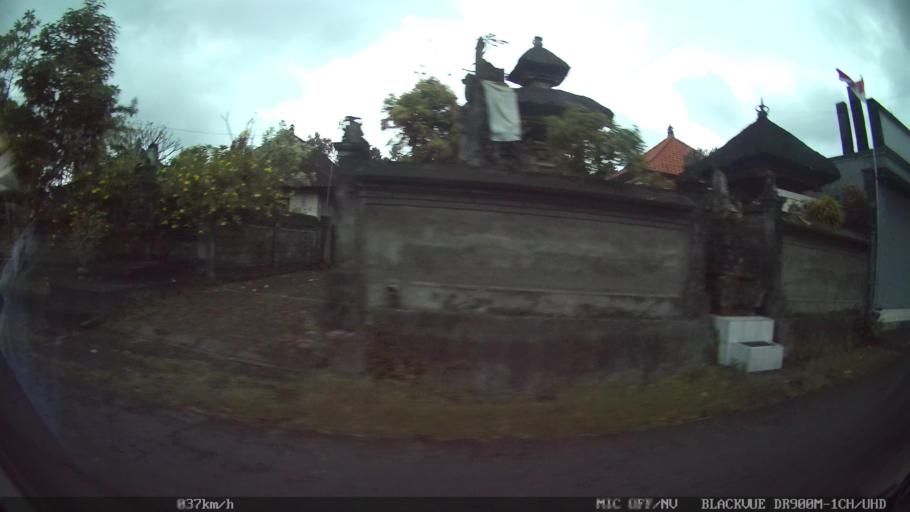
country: ID
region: Bali
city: Banjar Sempidi
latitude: -8.5239
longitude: 115.2015
